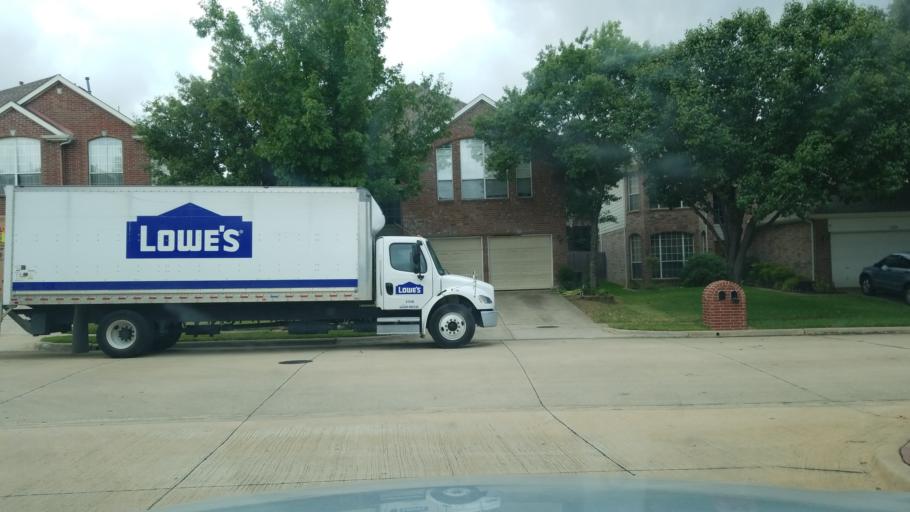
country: US
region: Texas
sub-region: Tarrant County
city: Euless
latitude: 32.8434
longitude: -97.1054
